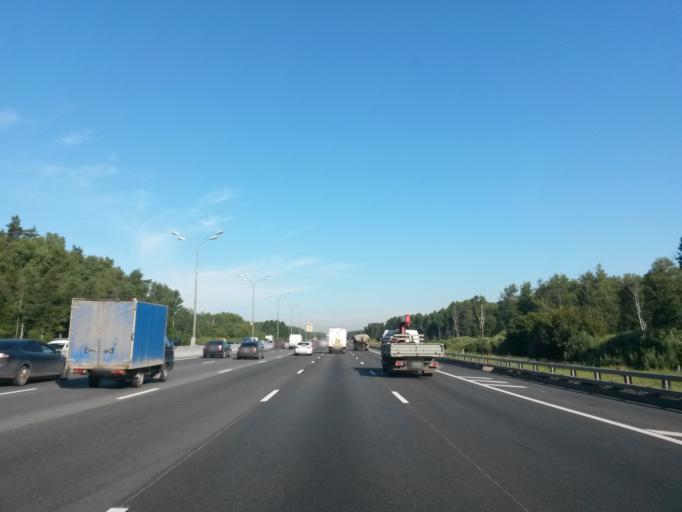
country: RU
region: Moskovskaya
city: Druzhba
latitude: 55.8632
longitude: 37.7636
